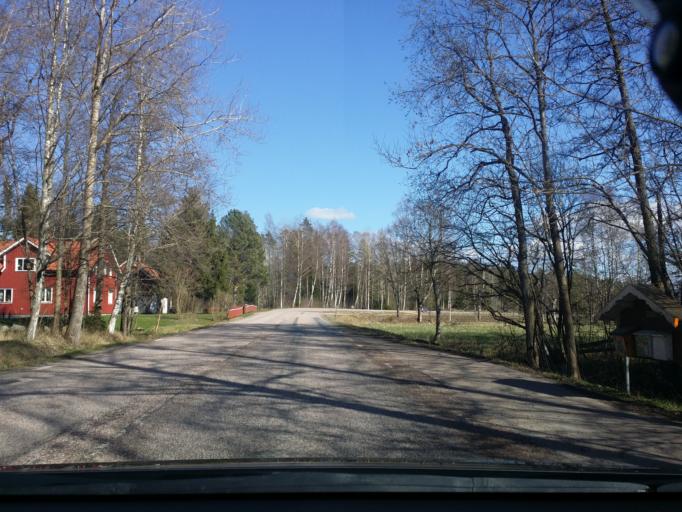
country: SE
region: Vaestmanland
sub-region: Sala Kommun
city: Sala
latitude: 59.9846
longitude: 16.4800
